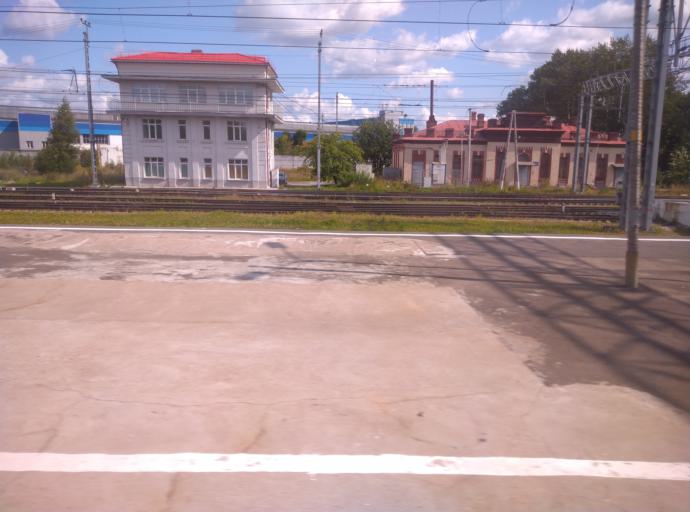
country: RU
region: St.-Petersburg
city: Obukhovo
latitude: 59.8492
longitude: 30.4538
